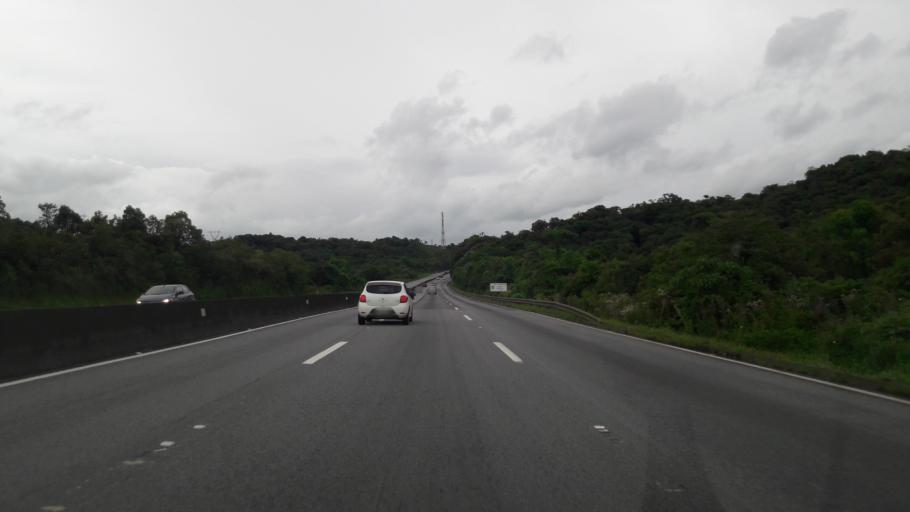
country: BR
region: Parana
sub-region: Piraquara
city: Piraquara
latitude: -25.5885
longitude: -48.9412
